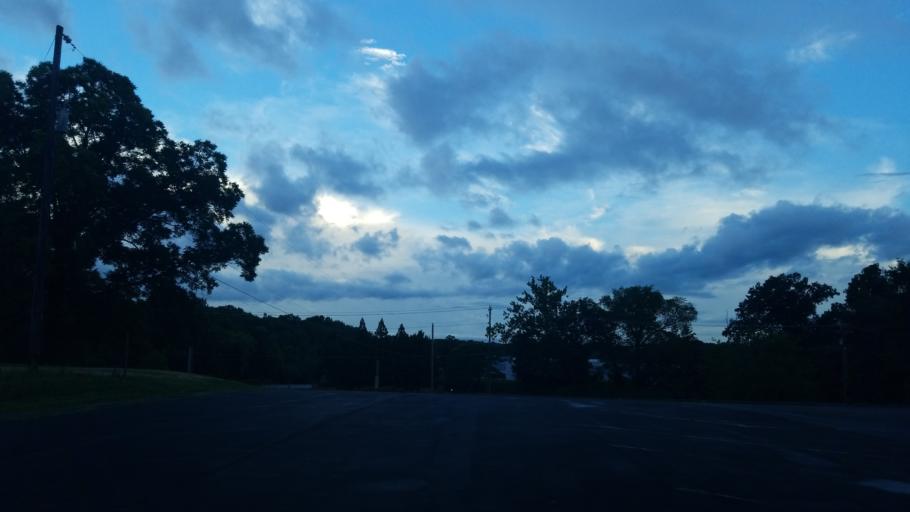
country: US
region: Tennessee
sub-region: Rutherford County
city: La Vergne
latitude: 36.1141
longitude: -86.6417
